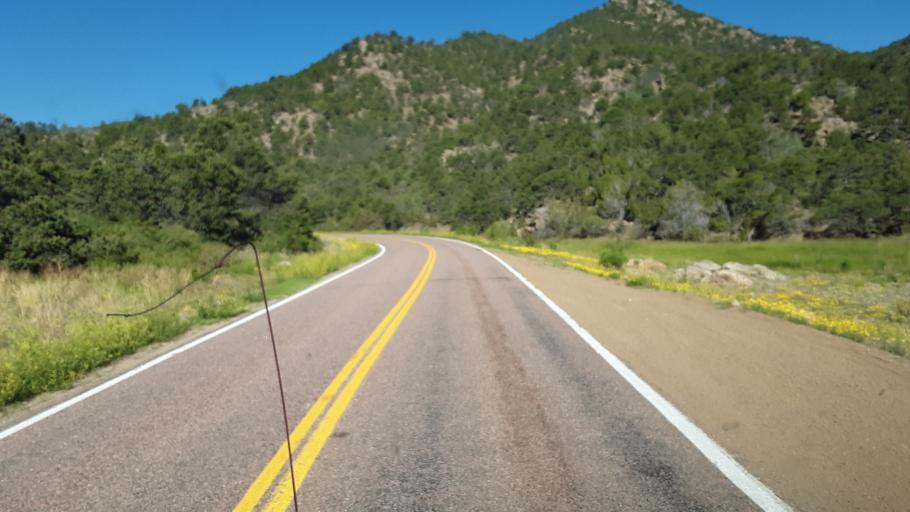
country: US
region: Colorado
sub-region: Fremont County
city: Canon City
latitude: 38.4279
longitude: -105.4011
